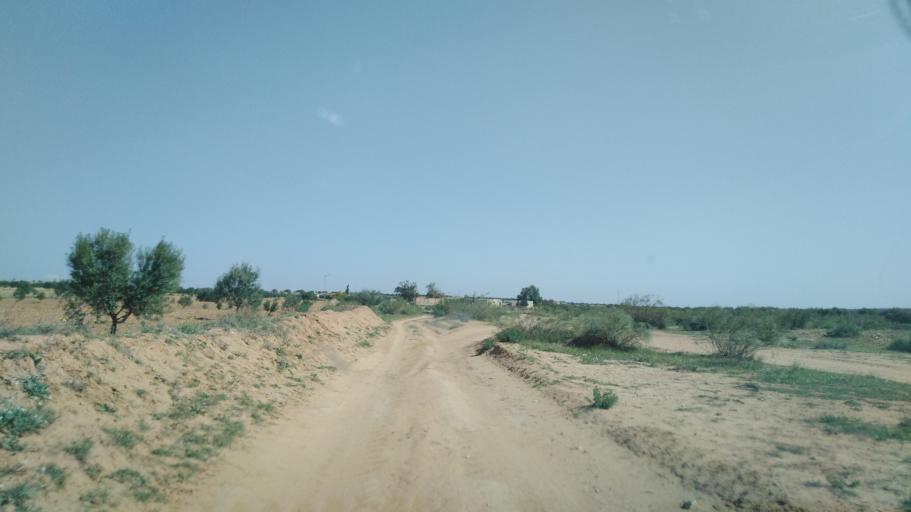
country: TN
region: Safaqis
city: Bi'r `Ali Bin Khalifah
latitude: 34.7803
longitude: 10.3642
